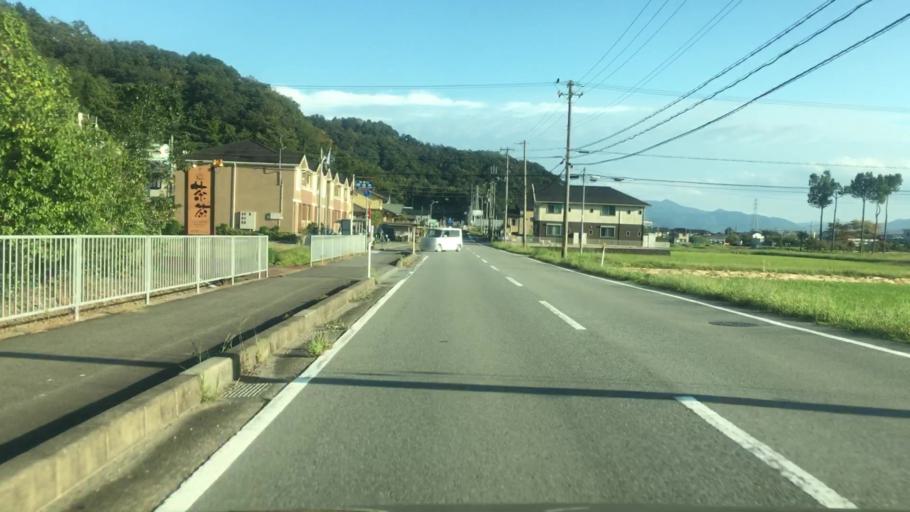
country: JP
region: Hyogo
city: Toyooka
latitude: 35.5626
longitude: 134.8214
